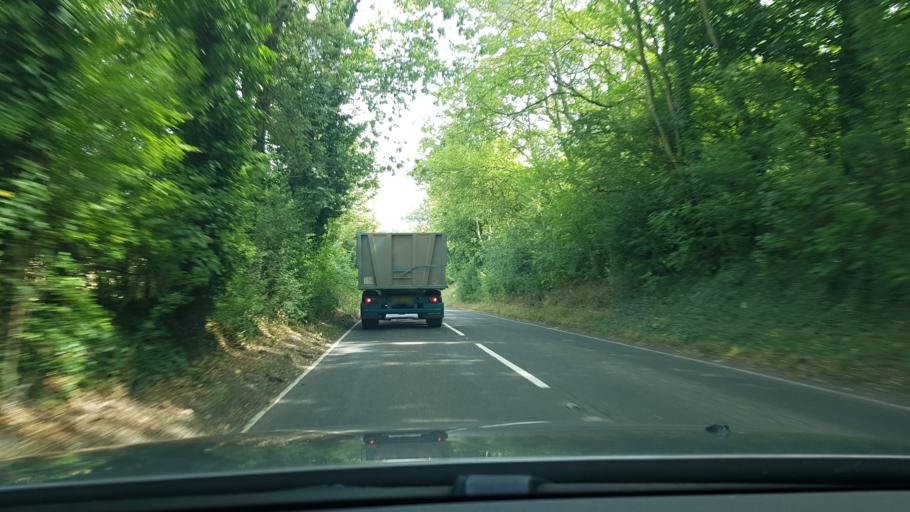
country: GB
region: England
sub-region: West Berkshire
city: Lambourn
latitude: 51.4977
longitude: -1.5415
